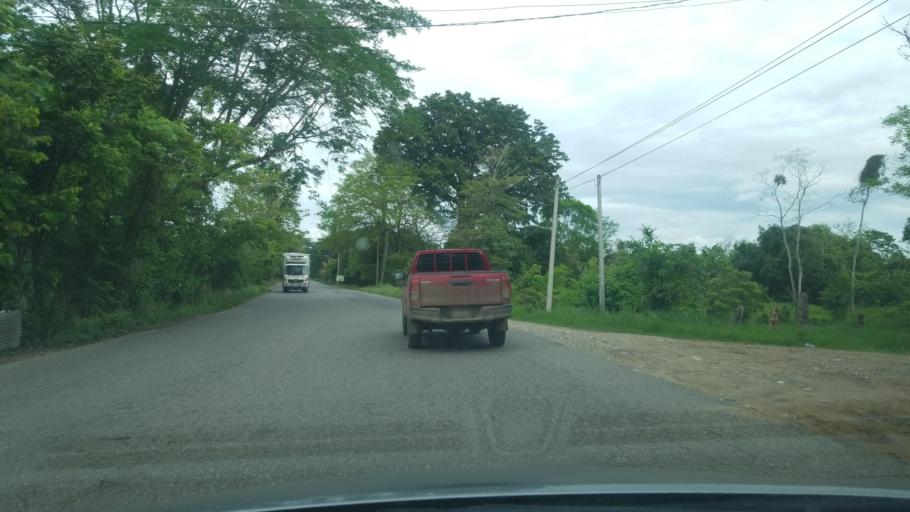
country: HN
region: Santa Barbara
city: La Flecha
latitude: 15.2995
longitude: -88.4736
